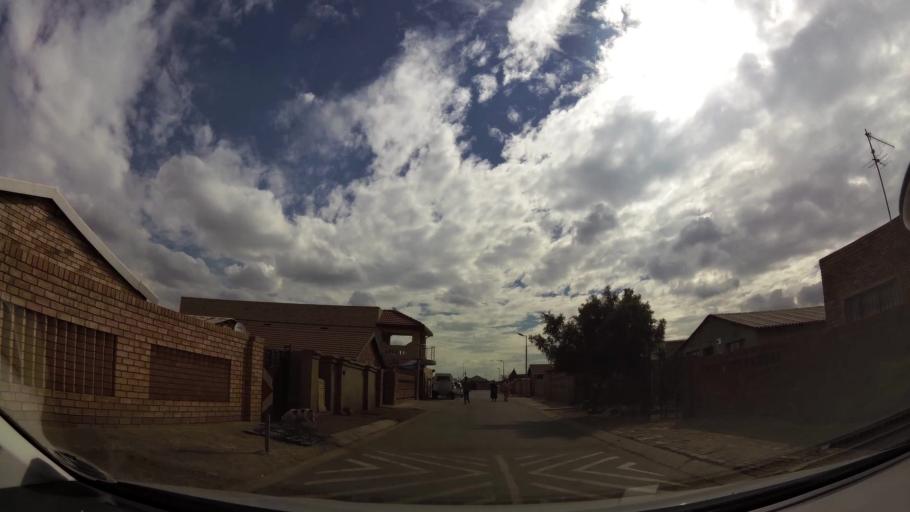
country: ZA
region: Gauteng
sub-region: City of Johannesburg Metropolitan Municipality
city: Soweto
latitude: -26.2762
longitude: 27.8467
